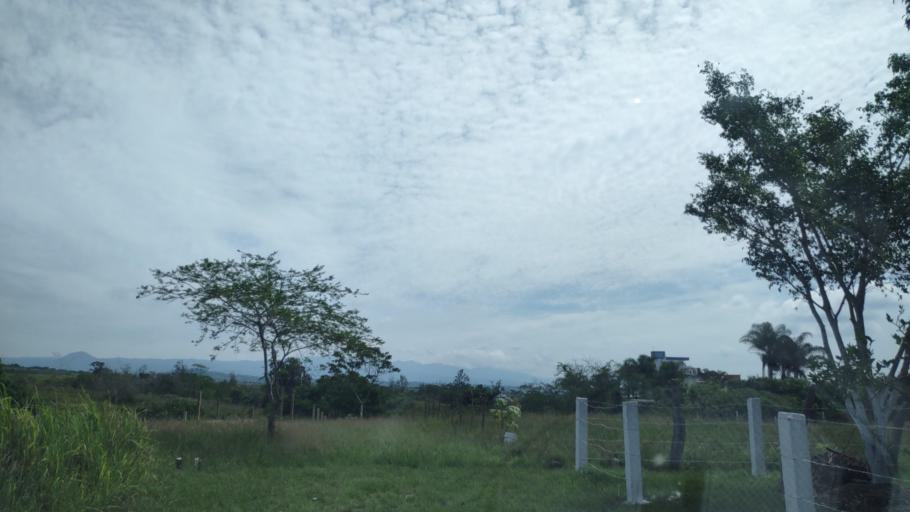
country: MX
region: Veracruz
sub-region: Emiliano Zapata
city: Jacarandas
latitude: 19.4733
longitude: -96.8310
